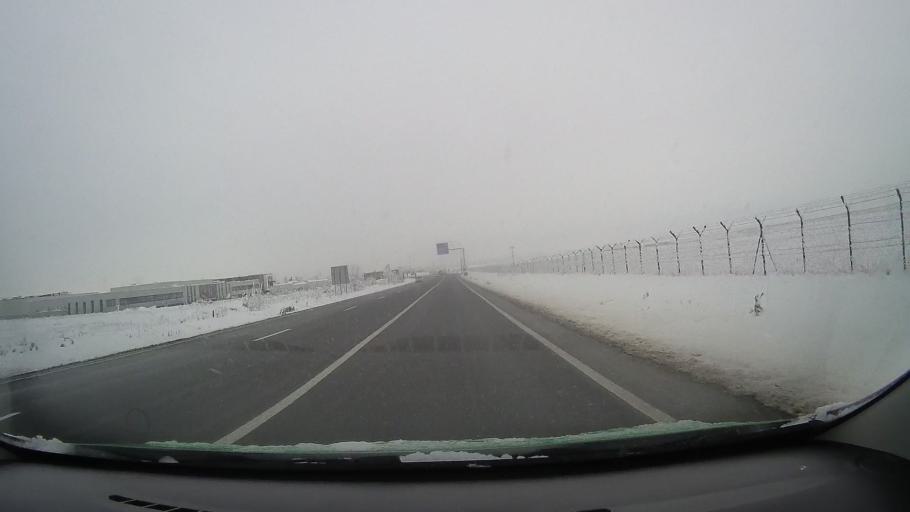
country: RO
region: Sibiu
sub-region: Comuna Cristian
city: Cristian
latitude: 45.7885
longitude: 24.0730
